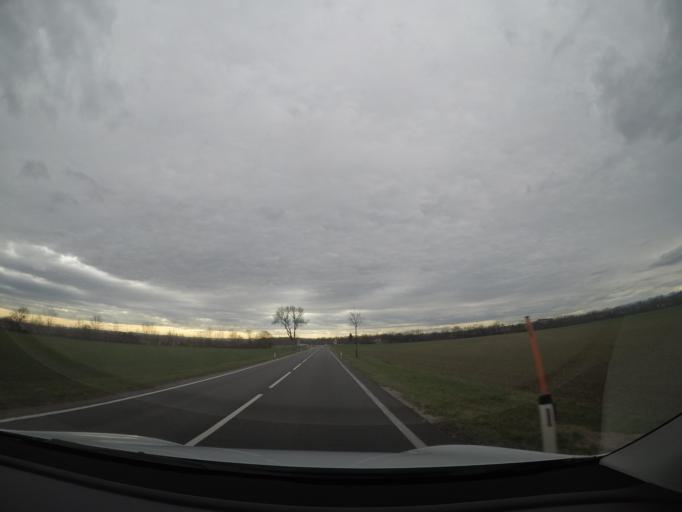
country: AT
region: Lower Austria
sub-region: Politischer Bezirk Modling
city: Biedermannsdorf
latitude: 48.0964
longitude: 16.3542
